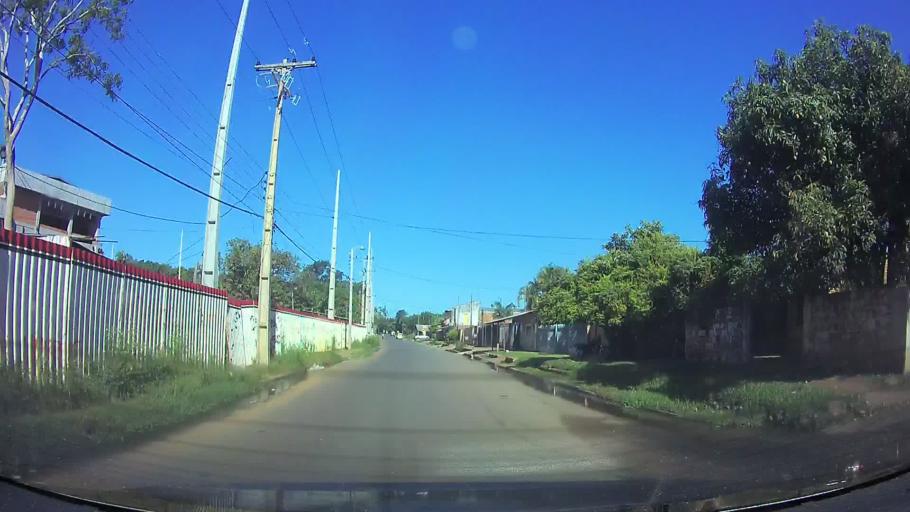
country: PY
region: Central
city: Fernando de la Mora
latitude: -25.2967
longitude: -57.5271
